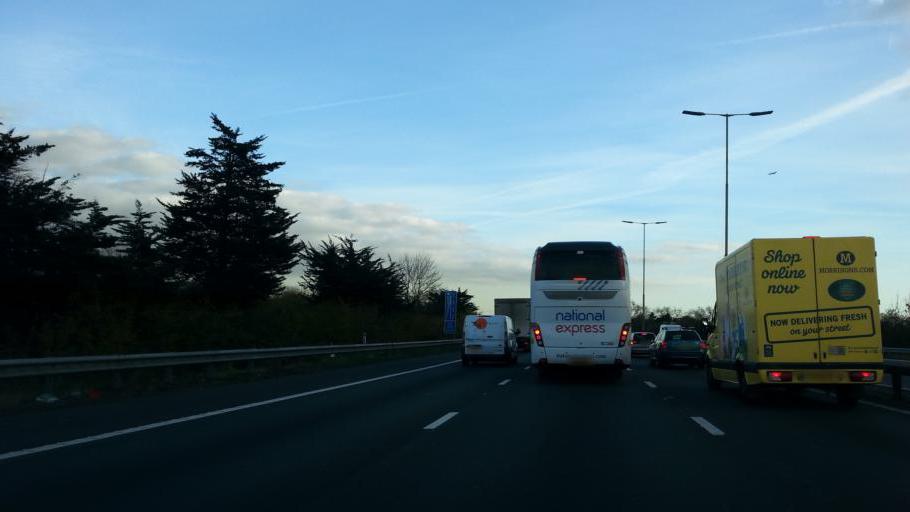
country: GB
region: England
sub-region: Royal Borough of Windsor and Maidenhead
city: Datchet
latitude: 51.4894
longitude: -0.5782
